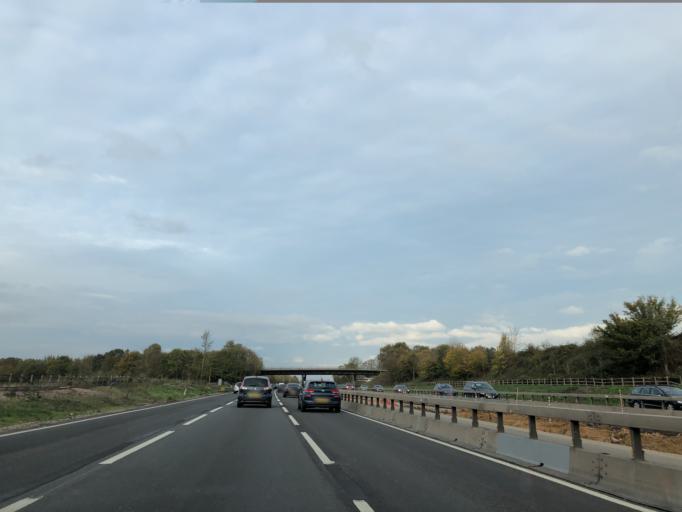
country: GB
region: England
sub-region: Royal Borough of Windsor and Maidenhead
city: White Waltham
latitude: 51.4783
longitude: -0.7649
